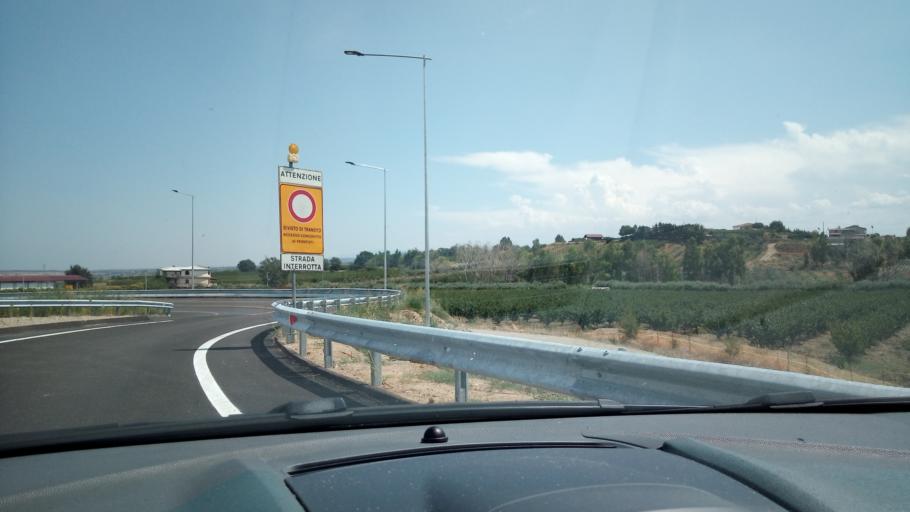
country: IT
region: Calabria
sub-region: Provincia di Cosenza
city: Firmo
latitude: 39.7190
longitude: 16.2321
